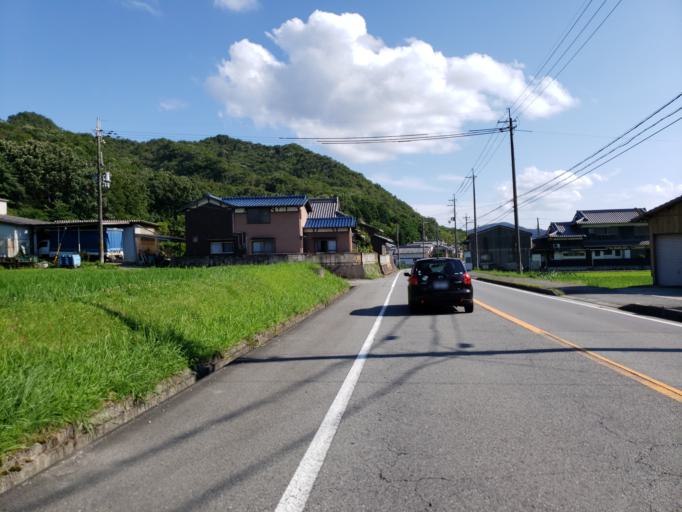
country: JP
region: Hyogo
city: Kakogawacho-honmachi
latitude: 34.8759
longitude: 134.7977
